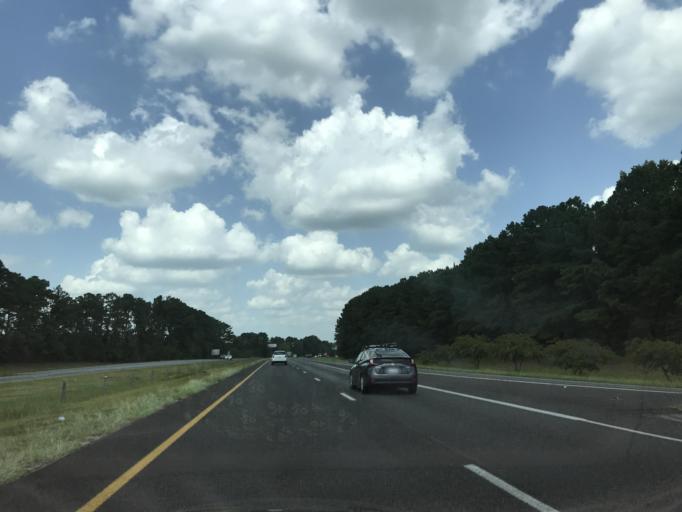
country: US
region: North Carolina
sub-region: Duplin County
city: Rose Hill
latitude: 34.8238
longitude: -77.9967
